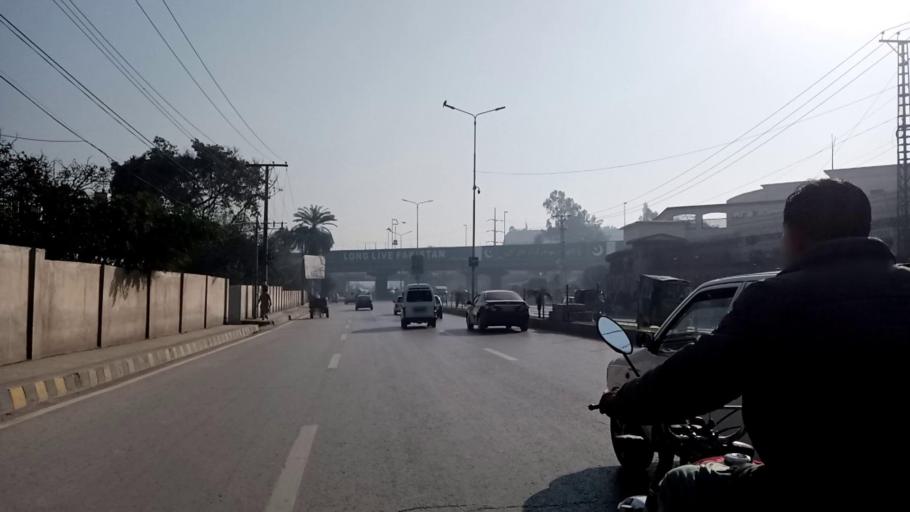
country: PK
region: Khyber Pakhtunkhwa
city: Peshawar
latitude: 34.0146
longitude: 71.5658
